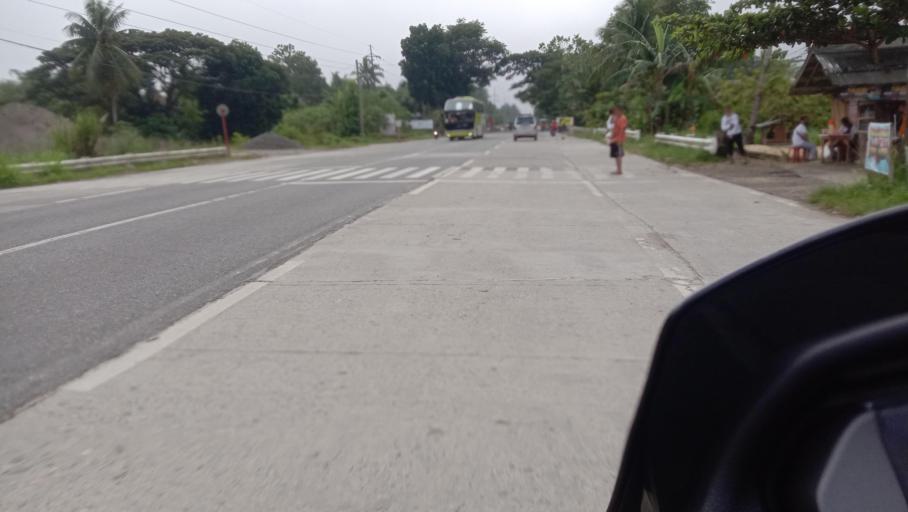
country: PH
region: Caraga
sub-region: Province of Agusan del Sur
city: Alegria
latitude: 8.5054
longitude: 125.9907
